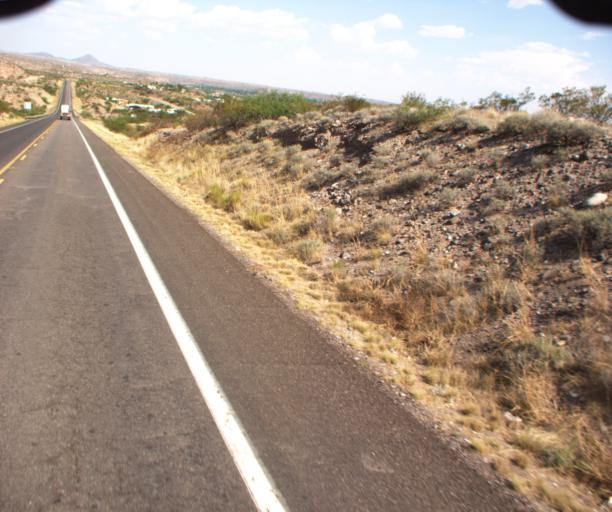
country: US
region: Arizona
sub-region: Greenlee County
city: Clifton
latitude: 32.9433
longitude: -109.2271
